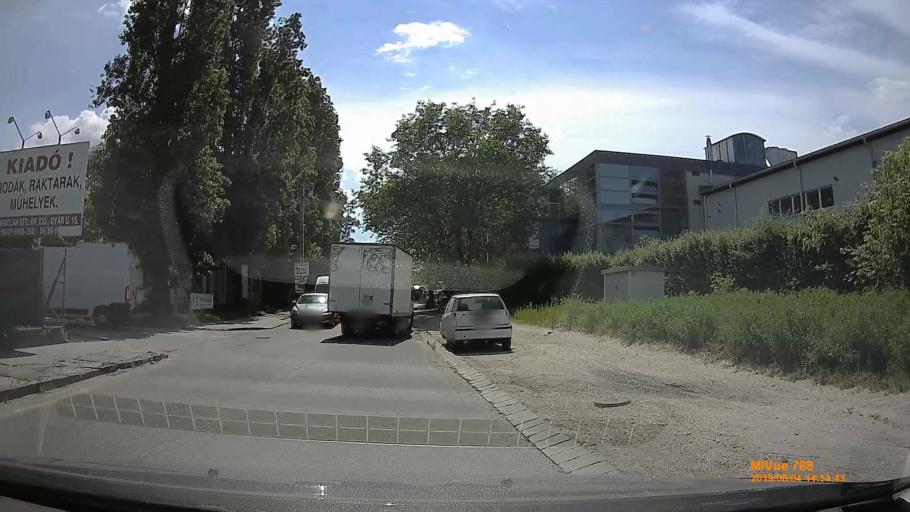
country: HU
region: Budapest
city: Budapest XXII. keruelet
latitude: 47.4103
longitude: 19.0345
